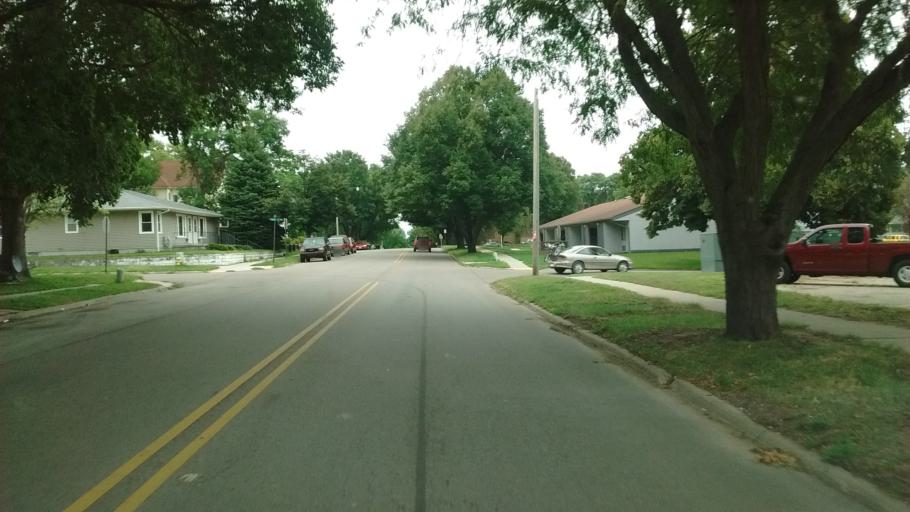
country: US
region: Iowa
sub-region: Woodbury County
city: Sioux City
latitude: 42.4995
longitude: -96.4189
